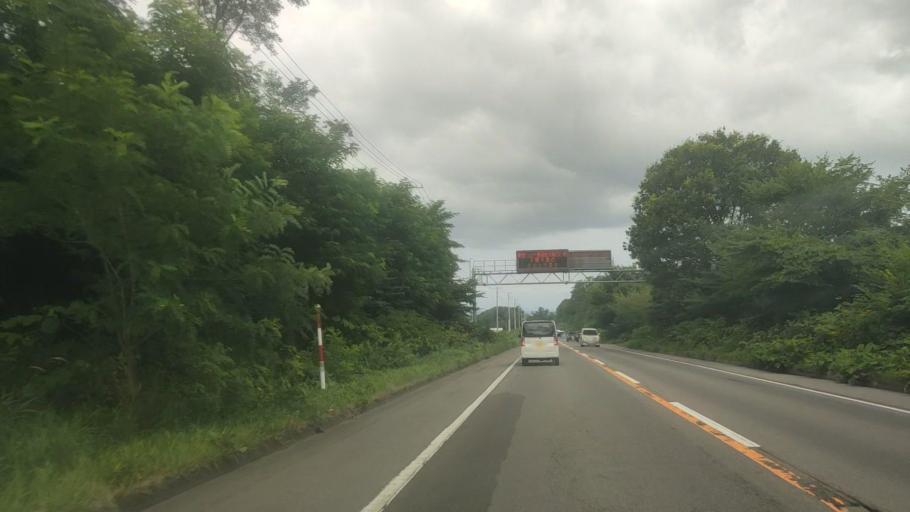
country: JP
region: Hokkaido
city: Nanae
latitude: 42.0736
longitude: 140.6016
